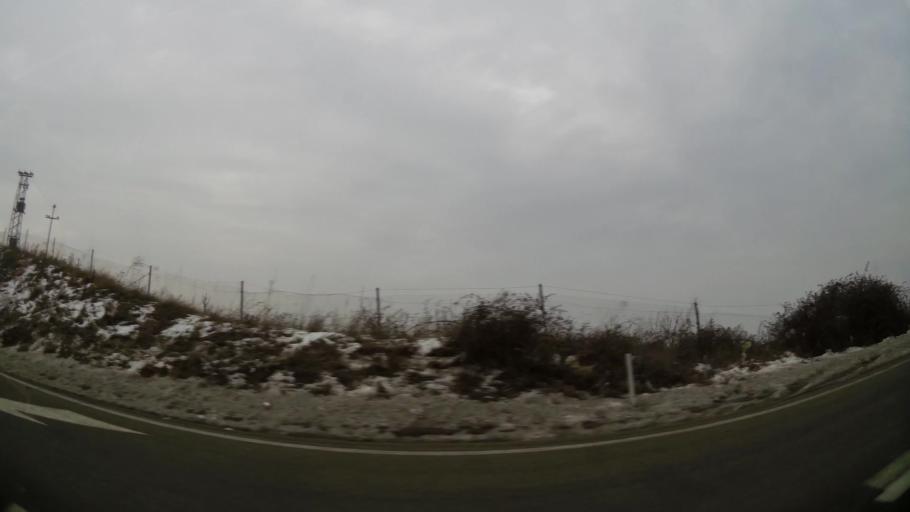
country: MK
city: Kondovo
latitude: 42.0431
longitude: 21.3377
